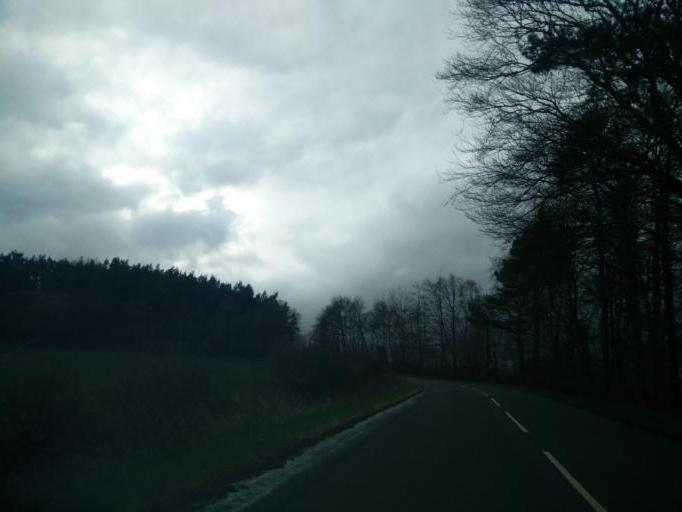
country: GB
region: England
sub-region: County Durham
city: Ushaw Moor
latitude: 54.7320
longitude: -1.6831
